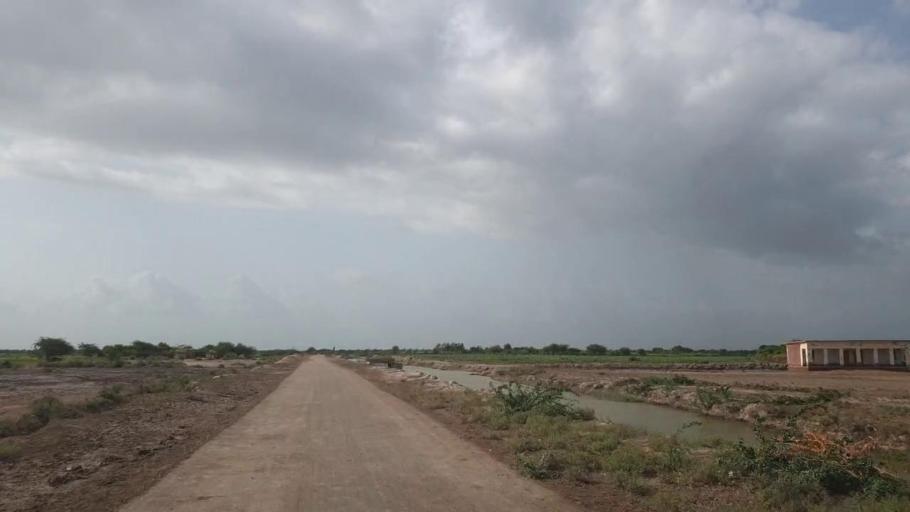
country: PK
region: Sindh
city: Kadhan
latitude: 24.5694
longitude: 69.0622
